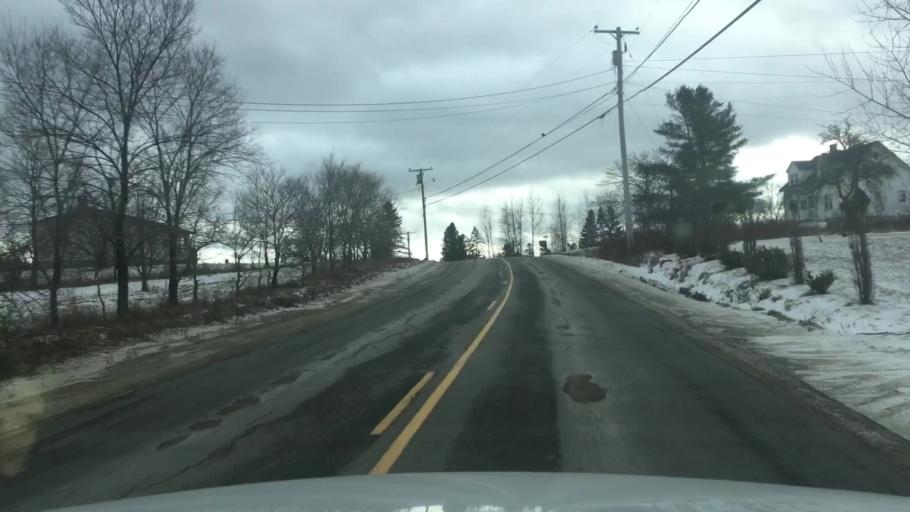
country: US
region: Maine
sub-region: Washington County
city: Machias
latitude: 44.6761
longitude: -67.4675
